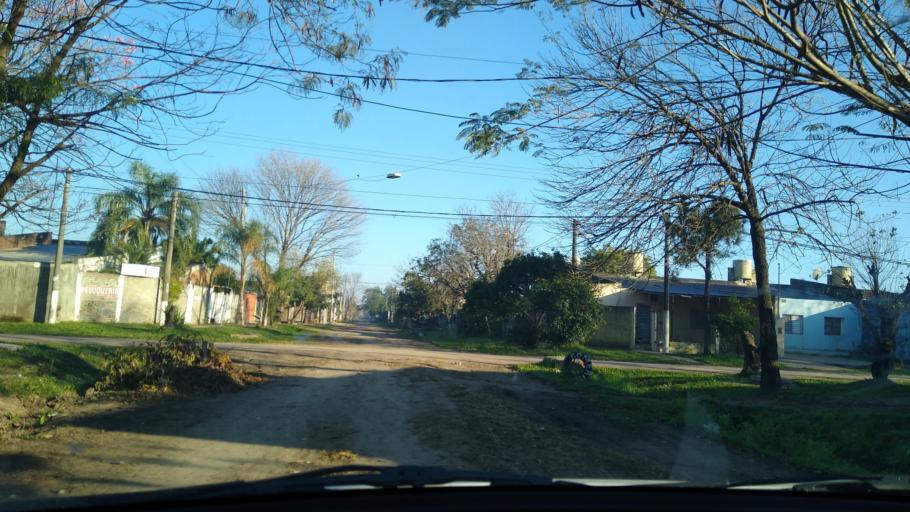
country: AR
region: Chaco
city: Resistencia
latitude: -27.4820
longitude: -58.9743
